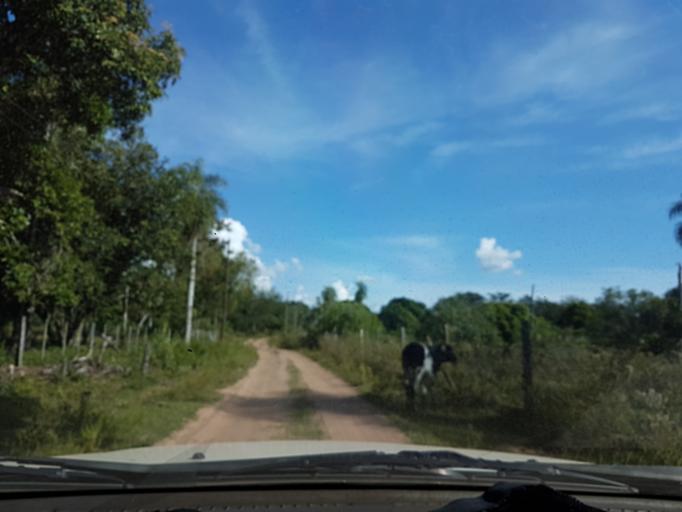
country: PY
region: Cordillera
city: Arroyos y Esteros
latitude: -24.9750
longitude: -57.1942
